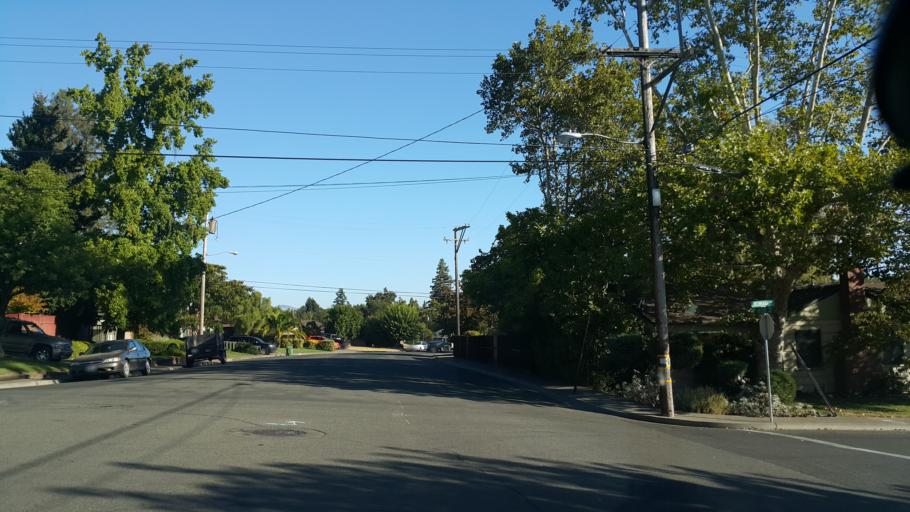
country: US
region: California
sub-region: Mendocino County
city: Ukiah
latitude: 39.1390
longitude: -123.2148
